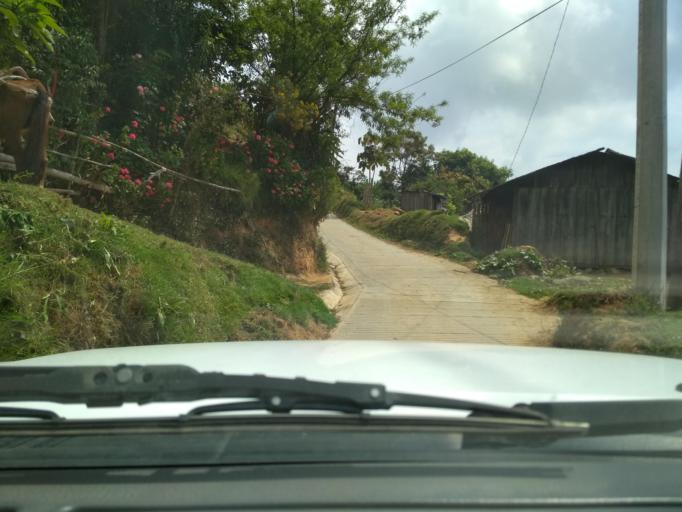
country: MX
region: Veracruz
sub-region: Camerino Z. Mendoza
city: Necoxtla
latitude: 18.7798
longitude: -97.1553
